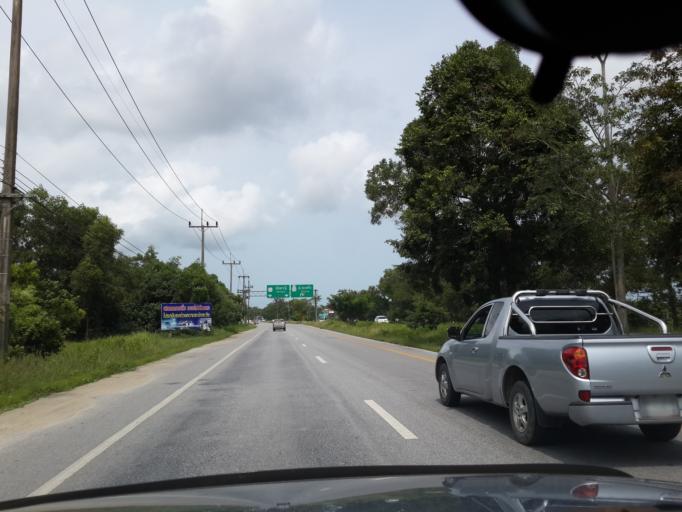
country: TH
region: Pattani
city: Yaring
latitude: 6.8518
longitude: 101.3778
